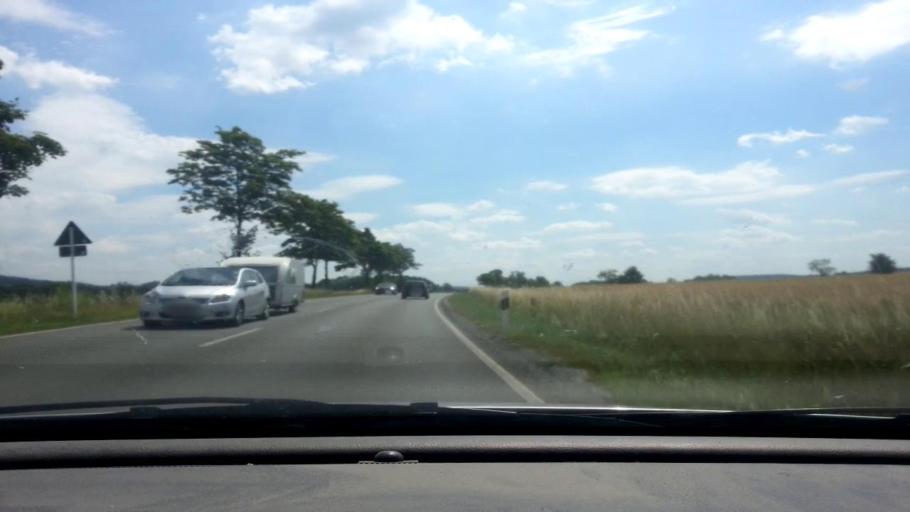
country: DE
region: Bavaria
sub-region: Upper Franconia
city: Neunkirchen am Main
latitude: 49.9179
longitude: 11.6479
